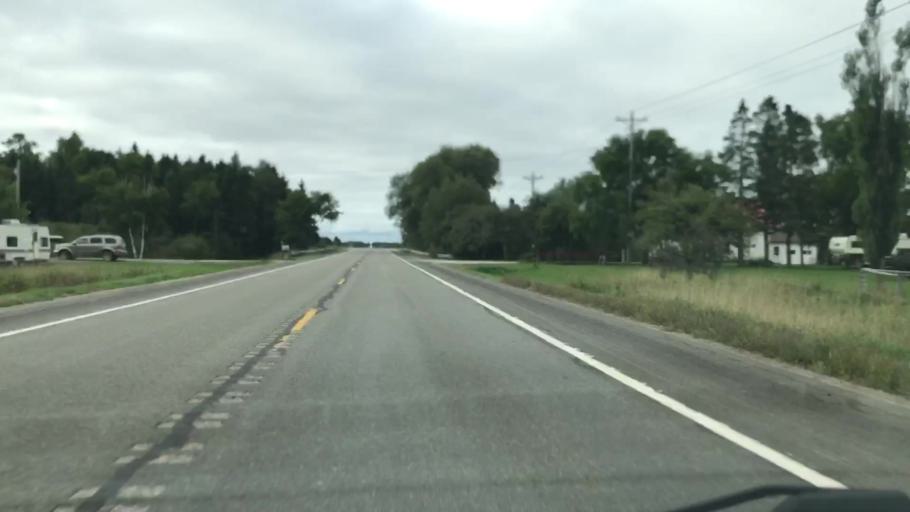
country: US
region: Michigan
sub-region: Luce County
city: Newberry
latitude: 46.1565
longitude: -85.5713
